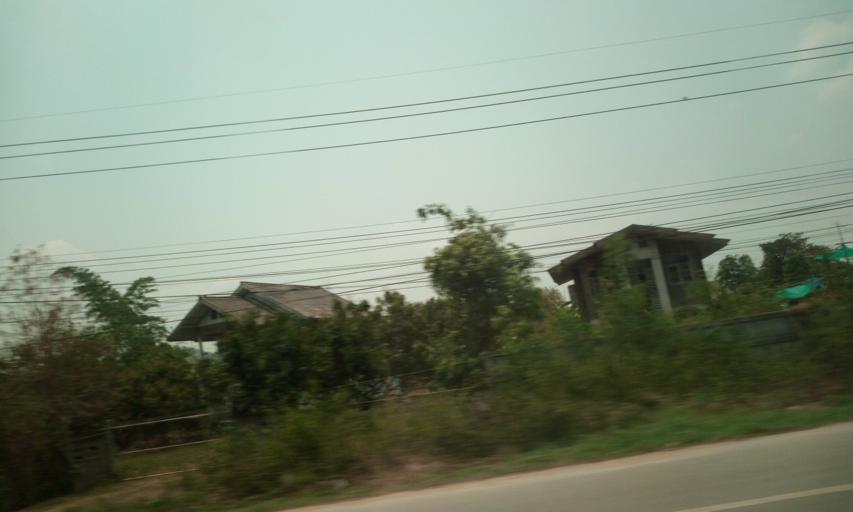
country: TH
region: Chiang Rai
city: Thoeng
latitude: 19.6842
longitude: 100.1310
